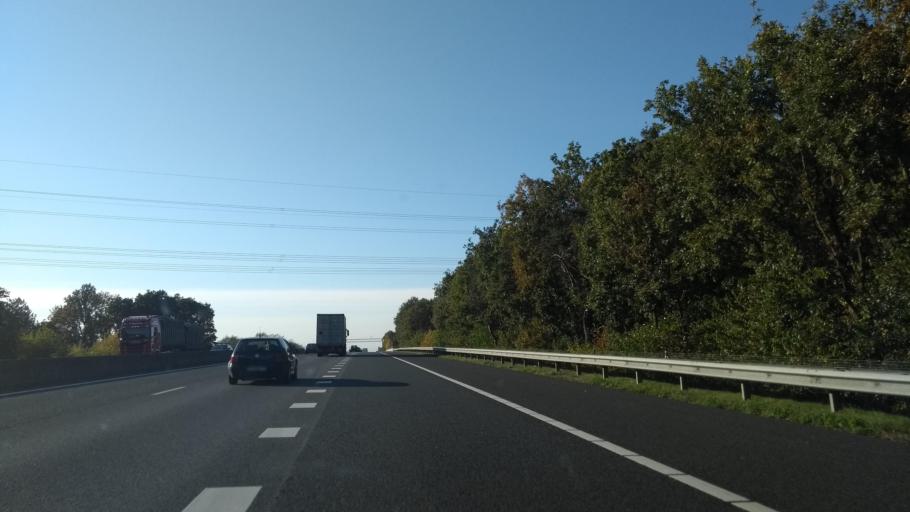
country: NL
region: Limburg
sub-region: Gemeente Venlo
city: Tegelen
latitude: 51.3936
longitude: 6.1141
